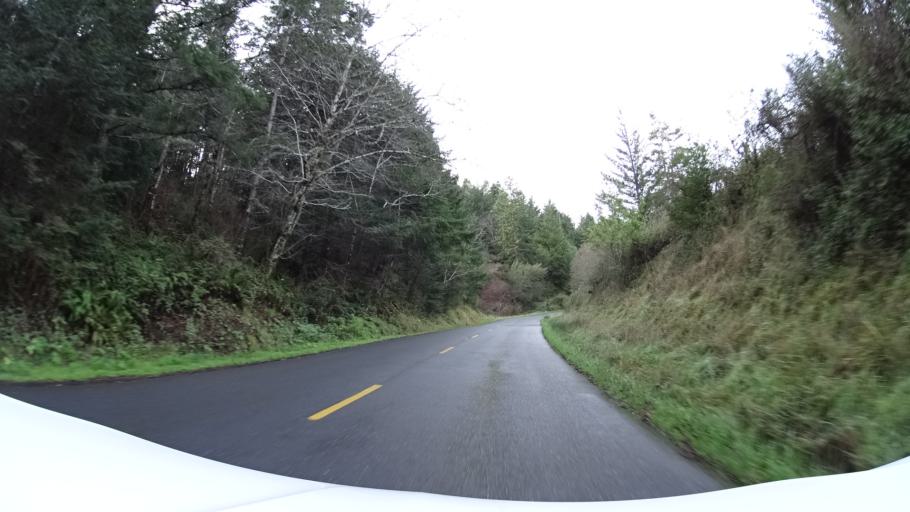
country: US
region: California
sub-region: Humboldt County
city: Ferndale
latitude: 40.3451
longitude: -124.3418
